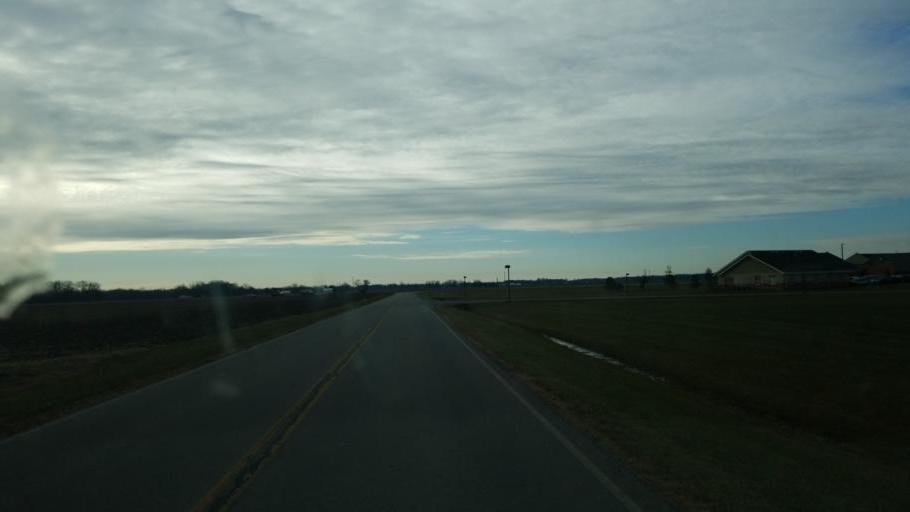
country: US
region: Ohio
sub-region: Marion County
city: Marion
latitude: 40.5867
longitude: -83.0102
